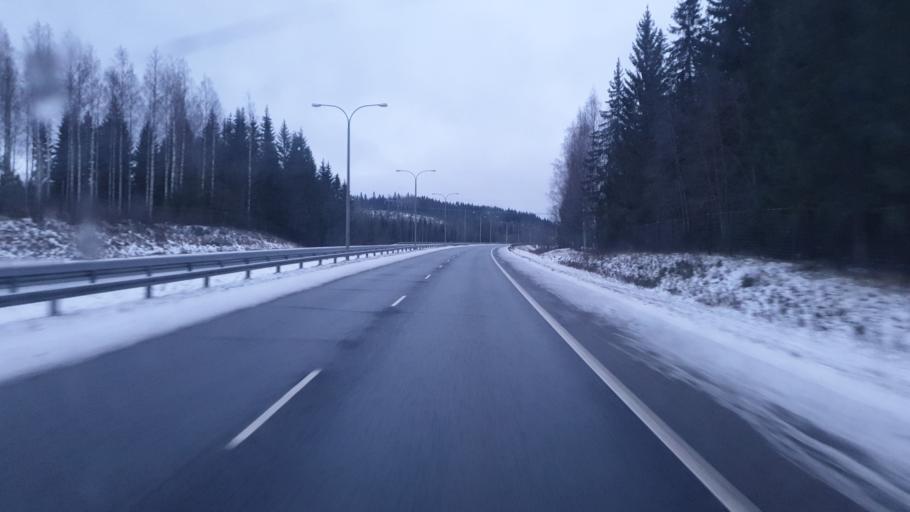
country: FI
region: Northern Savo
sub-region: Kuopio
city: Siilinjaervi
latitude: 63.0444
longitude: 27.6628
